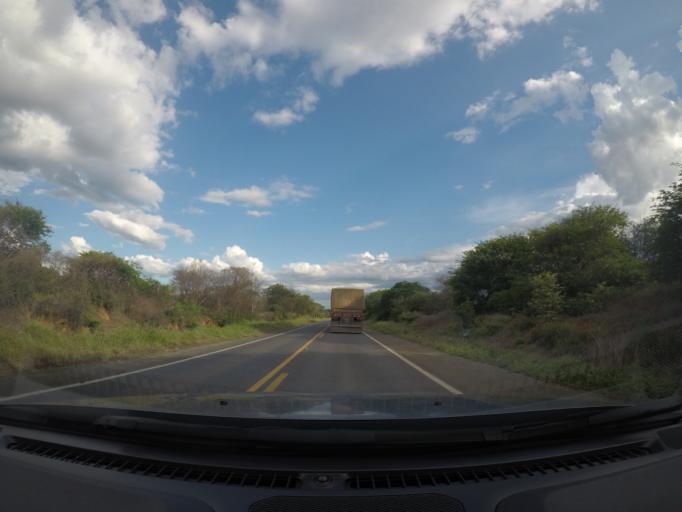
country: BR
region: Bahia
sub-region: Oliveira Dos Brejinhos
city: Beira Rio
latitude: -12.1836
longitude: -42.8311
